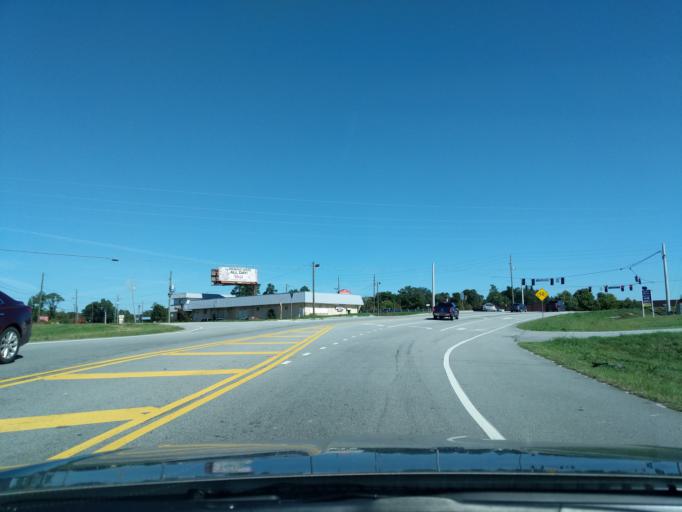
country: US
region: Georgia
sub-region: Richmond County
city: Augusta
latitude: 33.3654
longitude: -81.9966
